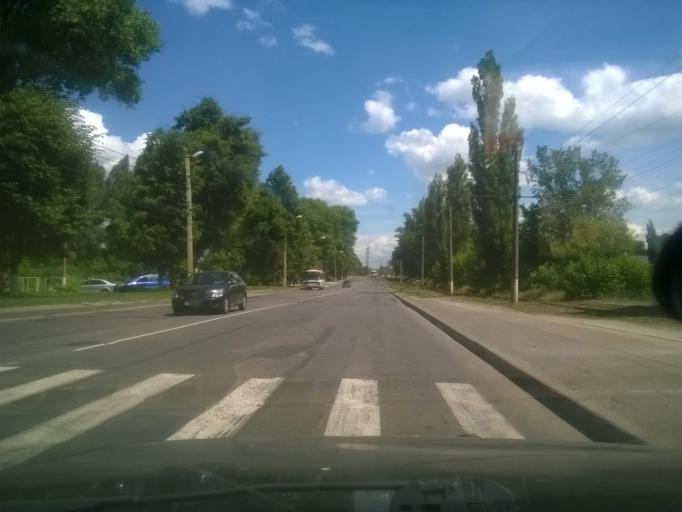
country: RU
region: Kursk
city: Voroshnevo
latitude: 51.6665
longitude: 36.1092
